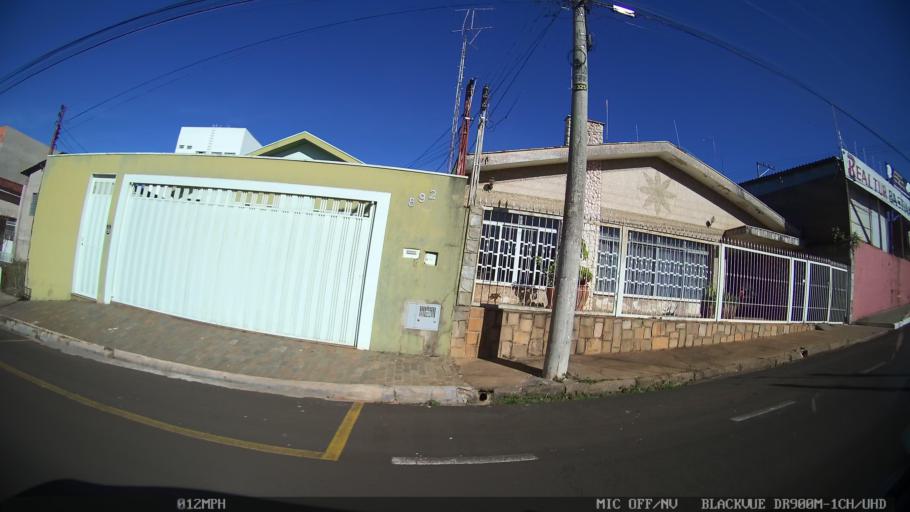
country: BR
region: Sao Paulo
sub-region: Franca
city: Franca
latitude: -20.5431
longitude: -47.4105
